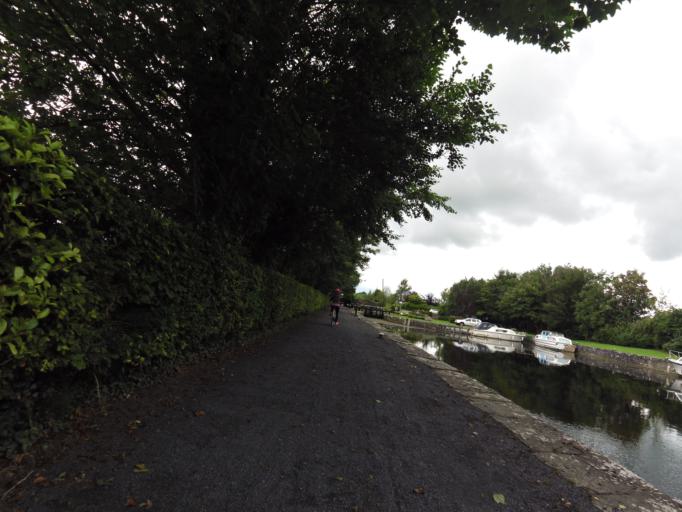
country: IE
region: Leinster
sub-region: An Iarmhi
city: An Muileann gCearr
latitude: 53.5342
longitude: -7.4670
